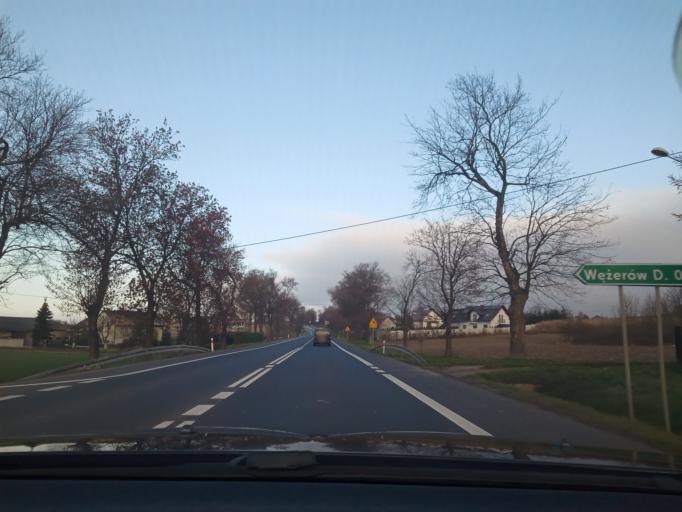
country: PL
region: Lesser Poland Voivodeship
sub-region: Powiat krakowski
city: Slomniki
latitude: 50.2873
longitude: 20.0511
